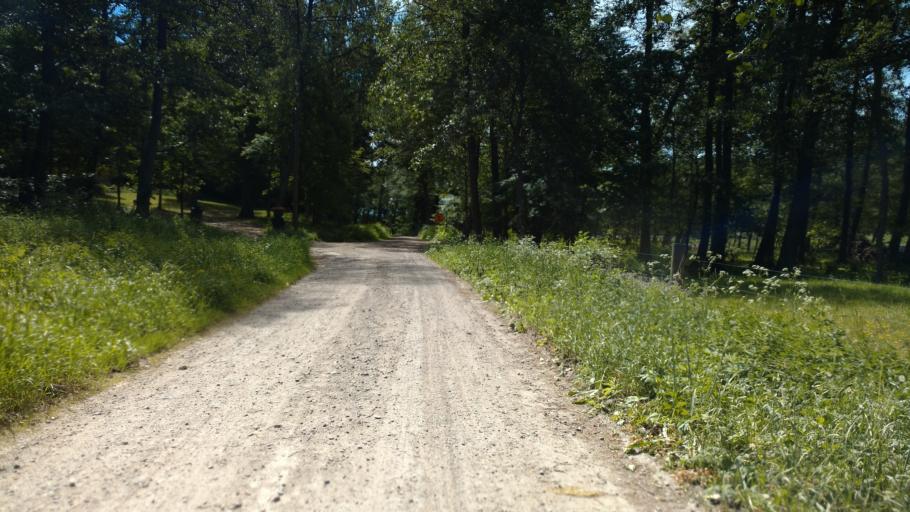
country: FI
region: Uusimaa
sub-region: Raaseporin
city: Pohja
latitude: 60.1216
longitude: 23.5389
